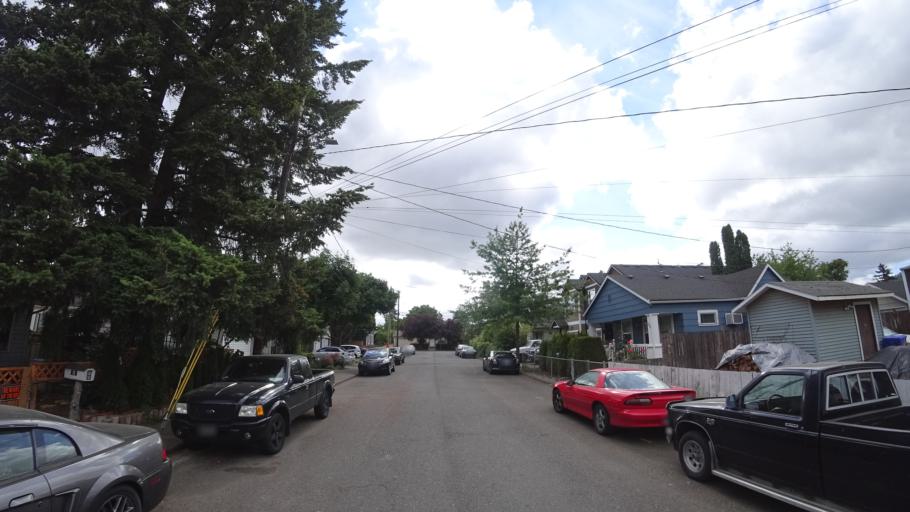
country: US
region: Oregon
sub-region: Multnomah County
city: Lents
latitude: 45.4794
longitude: -122.5644
